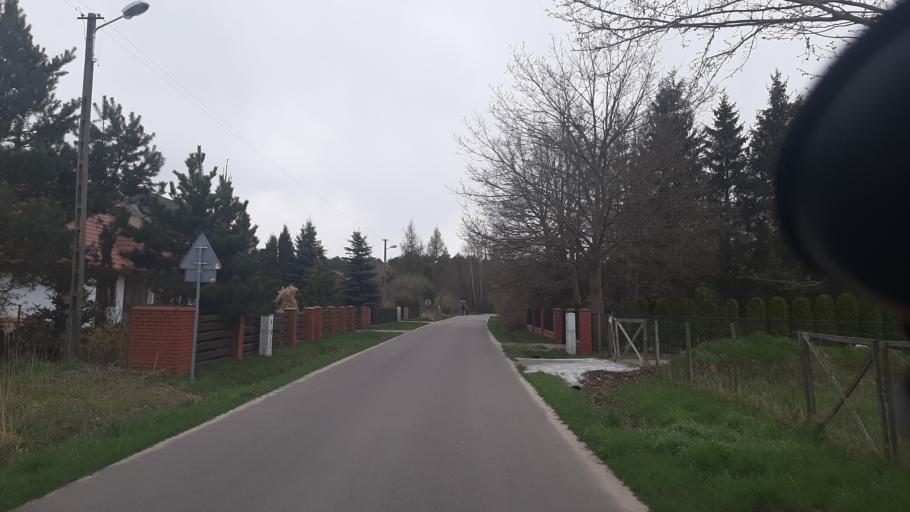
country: PL
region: Lublin Voivodeship
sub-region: Powiat lubelski
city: Niemce
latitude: 51.3826
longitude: 22.5570
